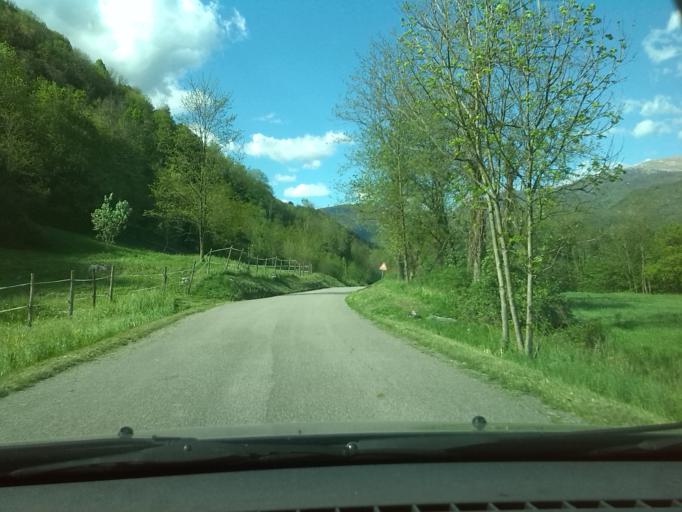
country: IT
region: Friuli Venezia Giulia
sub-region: Provincia di Udine
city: San Pietro al Natisone
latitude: 46.1344
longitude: 13.4820
